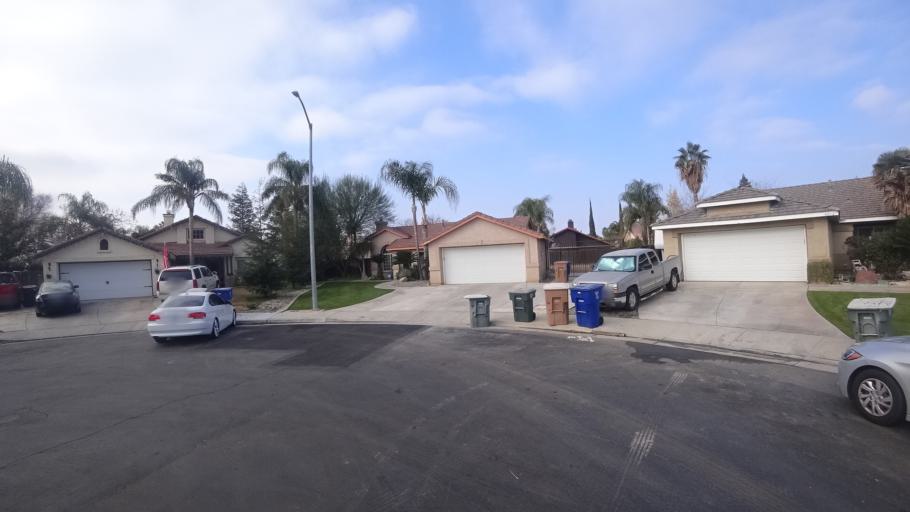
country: US
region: California
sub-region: Kern County
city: Greenfield
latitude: 35.3012
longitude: -119.0696
